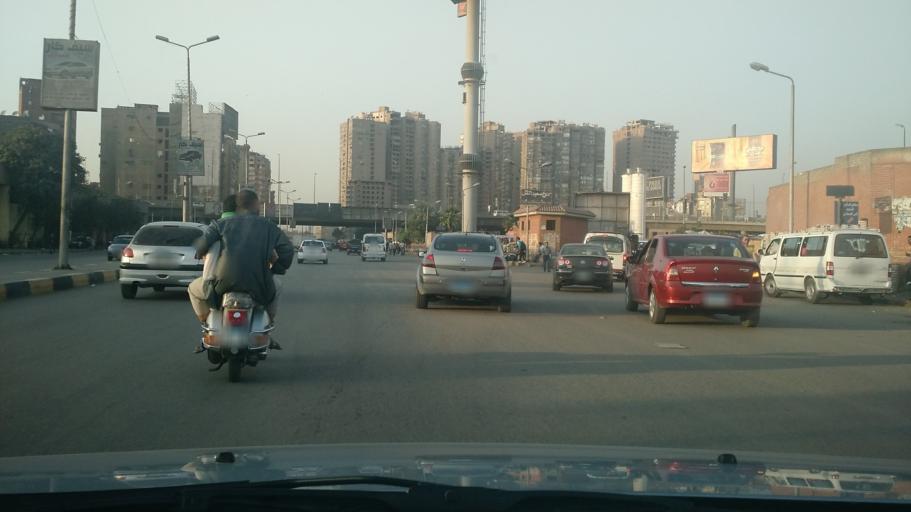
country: EG
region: Al Jizah
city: Al Jizah
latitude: 29.9847
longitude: 31.2130
